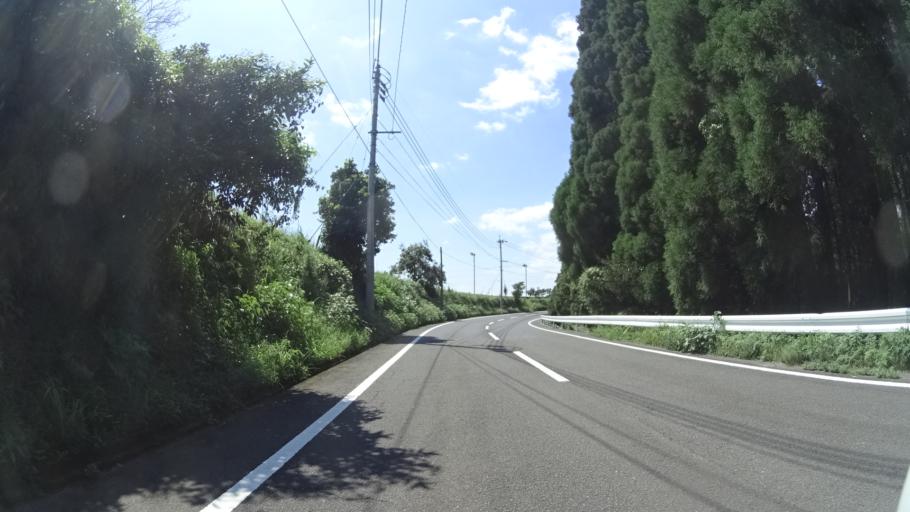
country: JP
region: Kagoshima
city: Kajiki
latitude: 31.8192
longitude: 130.7145
